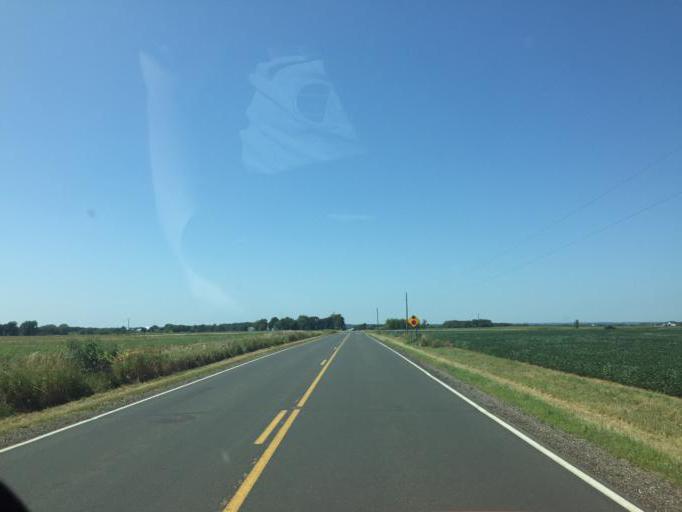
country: US
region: Minnesota
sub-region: Olmsted County
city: Rochester
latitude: 43.9640
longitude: -92.5146
